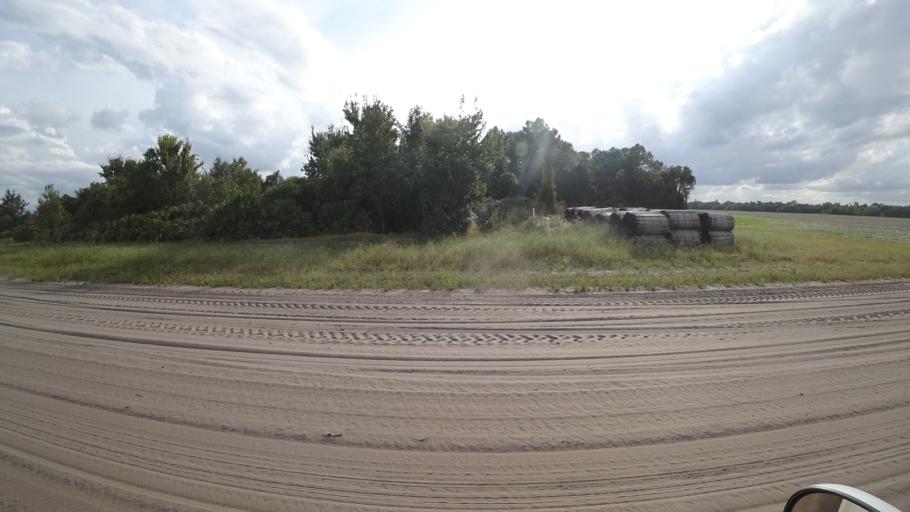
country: US
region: Florida
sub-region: Hillsborough County
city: Wimauma
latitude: 27.6068
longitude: -82.1436
